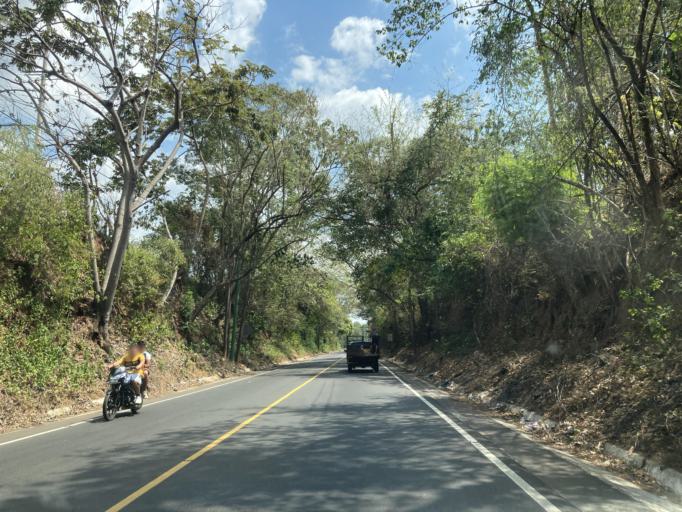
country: GT
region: Santa Rosa
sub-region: Municipio de Taxisco
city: Taxisco
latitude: 14.0642
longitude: -90.4511
